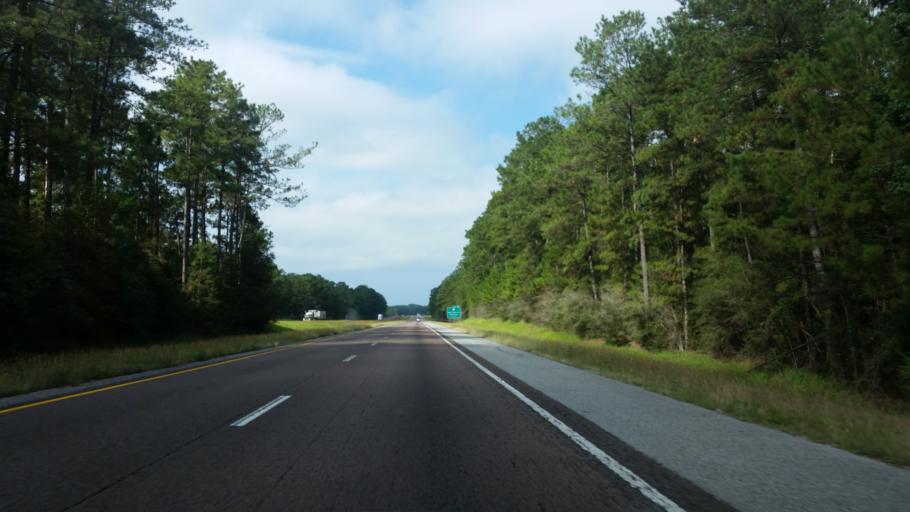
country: US
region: Alabama
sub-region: Baldwin County
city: Bay Minette
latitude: 30.9569
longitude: -87.8089
